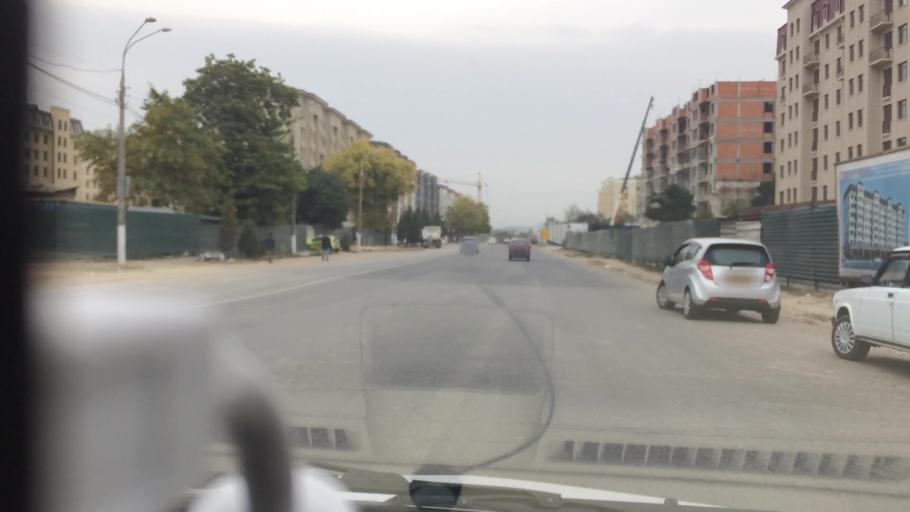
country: UZ
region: Toshkent
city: Salor
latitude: 41.3117
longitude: 69.3330
